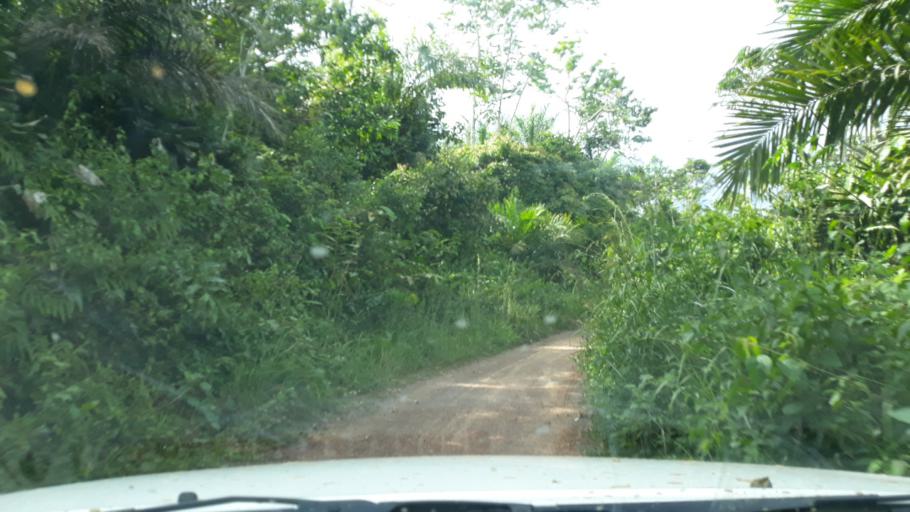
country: CD
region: Maniema
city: Kampene
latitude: -2.7586
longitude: 26.9273
